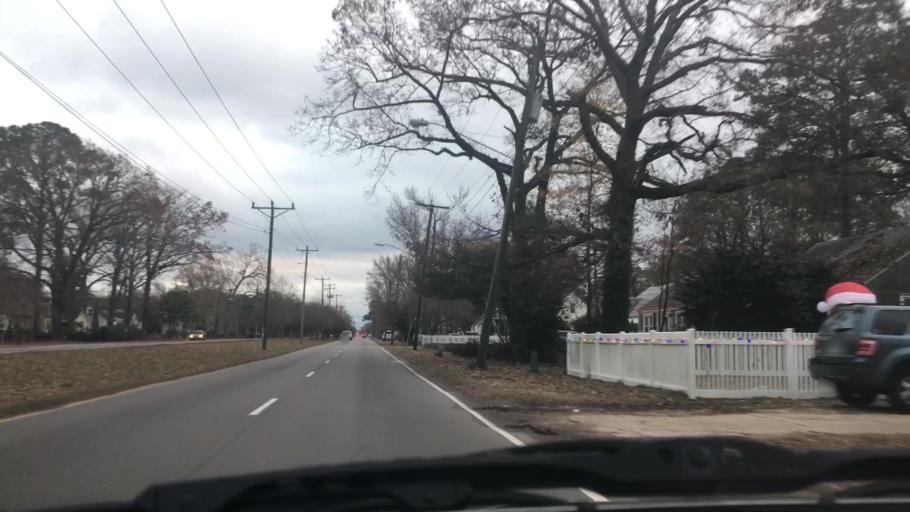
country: US
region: Virginia
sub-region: City of Norfolk
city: Norfolk
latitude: 36.9234
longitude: -76.2430
